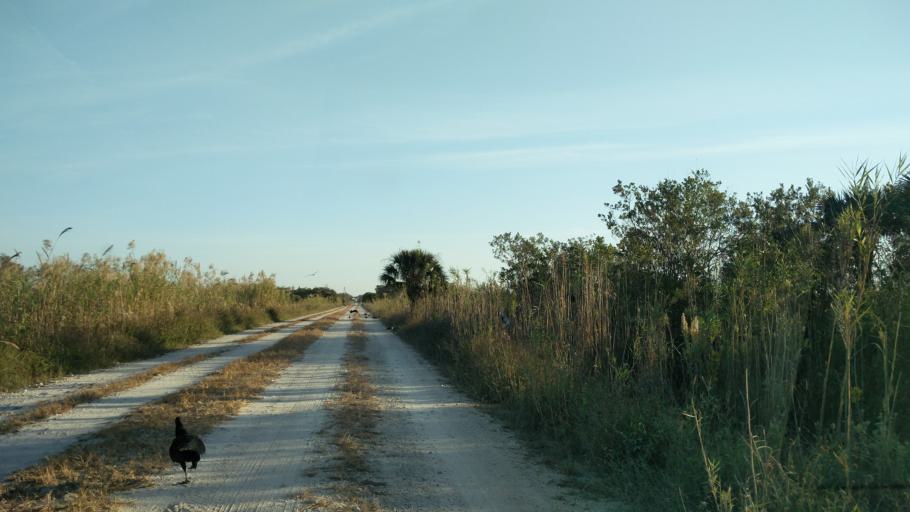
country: US
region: Florida
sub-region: Collier County
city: Lely Resort
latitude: 25.9651
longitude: -81.3657
